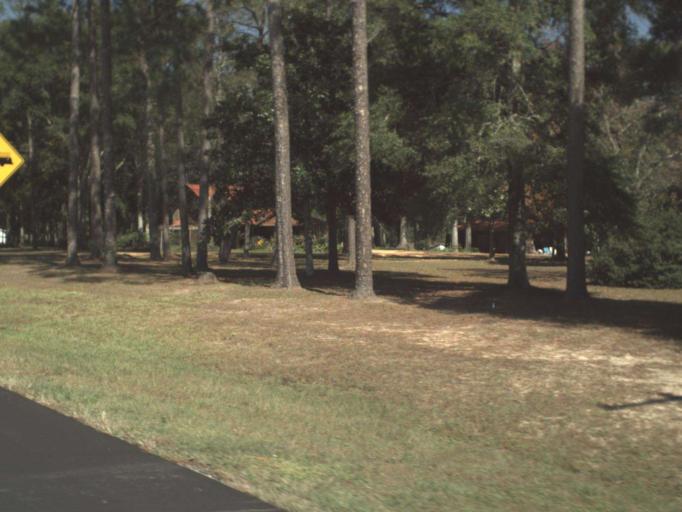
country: US
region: Alabama
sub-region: Covington County
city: Florala
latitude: 30.9674
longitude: -86.3011
